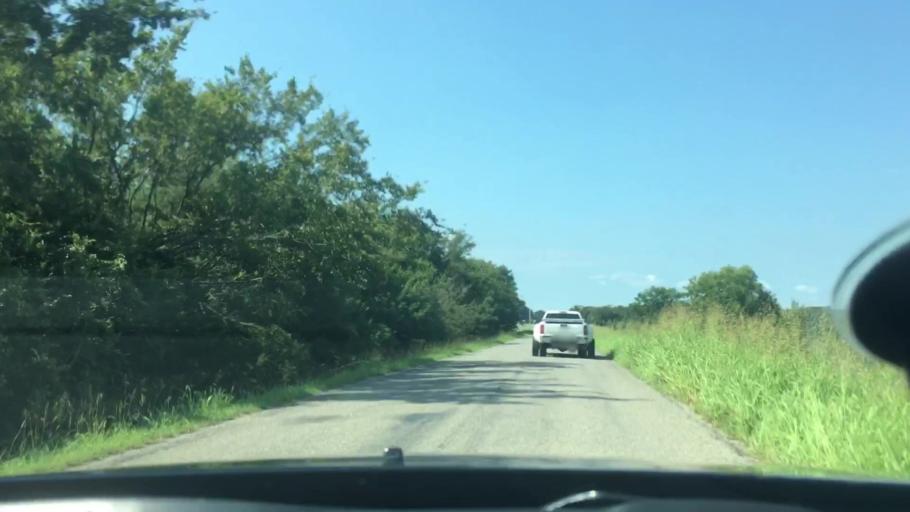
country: US
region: Oklahoma
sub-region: Bryan County
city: Colbert
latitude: 33.8984
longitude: -96.5471
